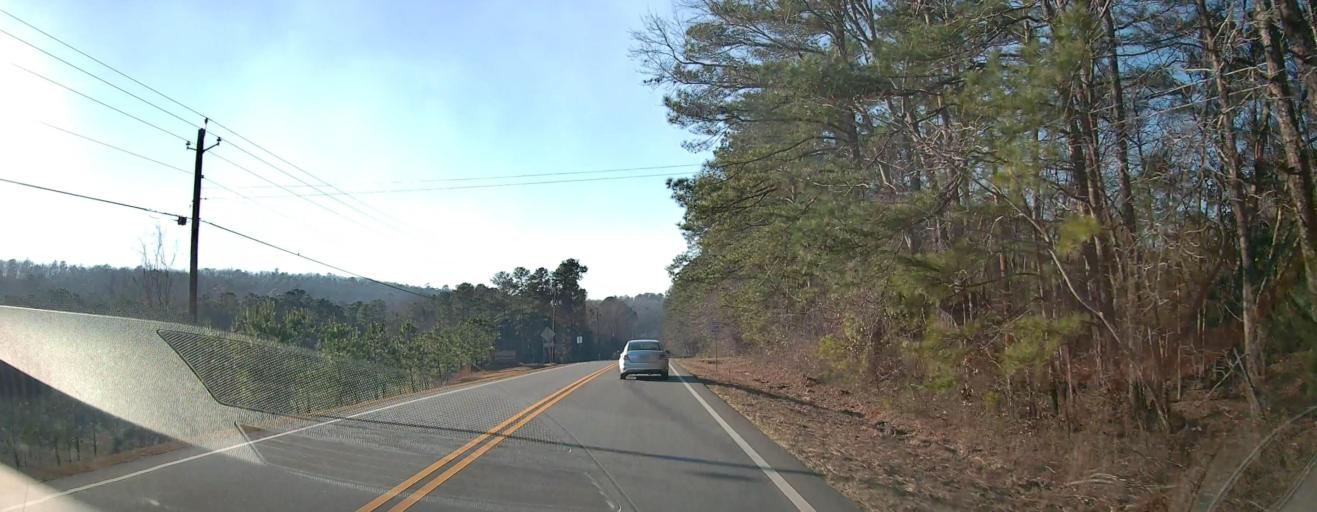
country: US
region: Georgia
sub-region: Meriwether County
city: Manchester
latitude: 32.8807
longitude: -84.6674
